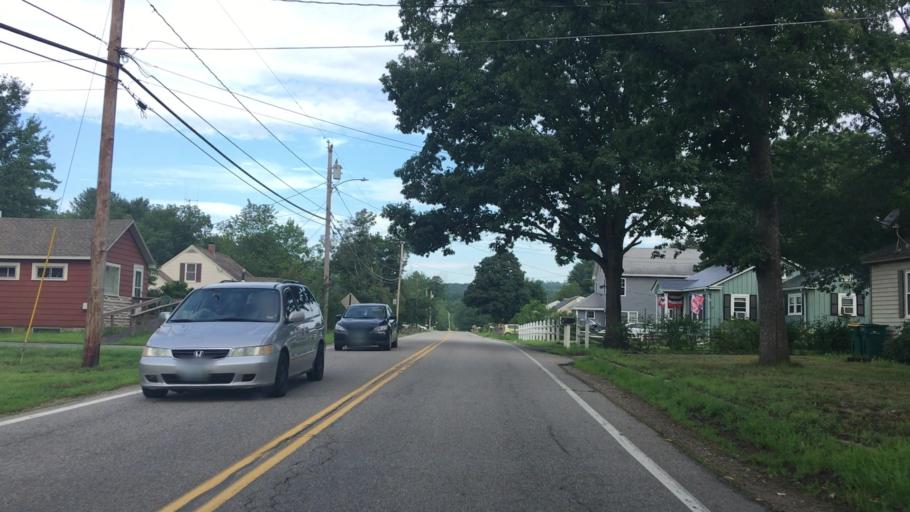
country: US
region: New Hampshire
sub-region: Strafford County
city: Rochester
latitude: 43.3485
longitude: -70.9763
